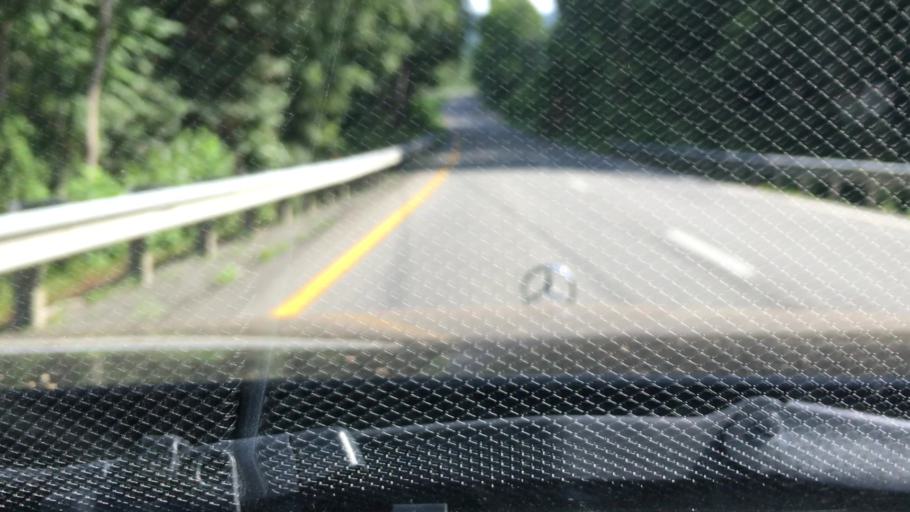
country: US
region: Virginia
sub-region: Albemarle County
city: Crozet
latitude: 37.9077
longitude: -78.6917
